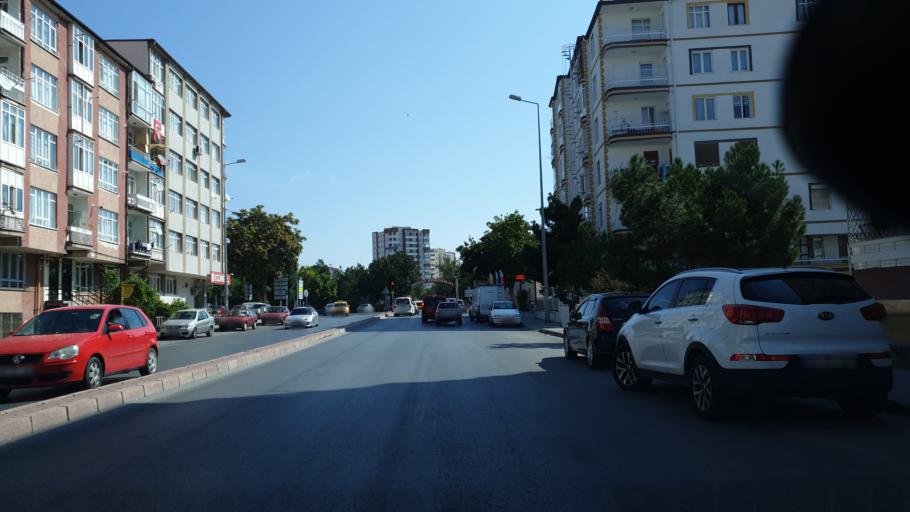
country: TR
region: Kayseri
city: Kayseri
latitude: 38.7391
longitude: 35.4902
